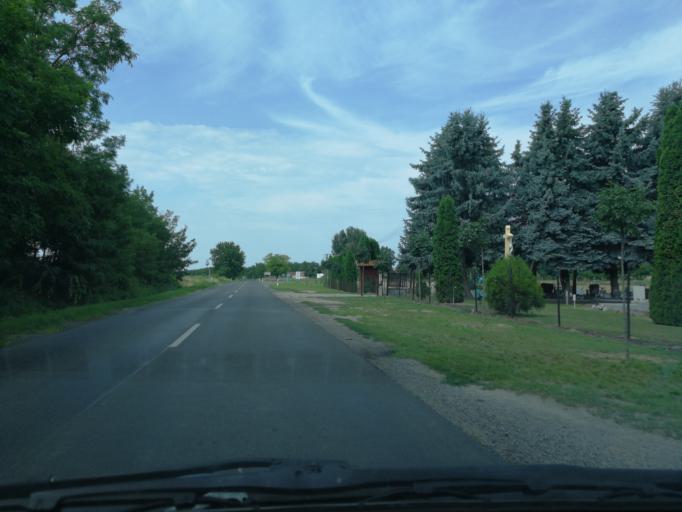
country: HU
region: Bacs-Kiskun
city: Davod
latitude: 46.0040
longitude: 18.9293
